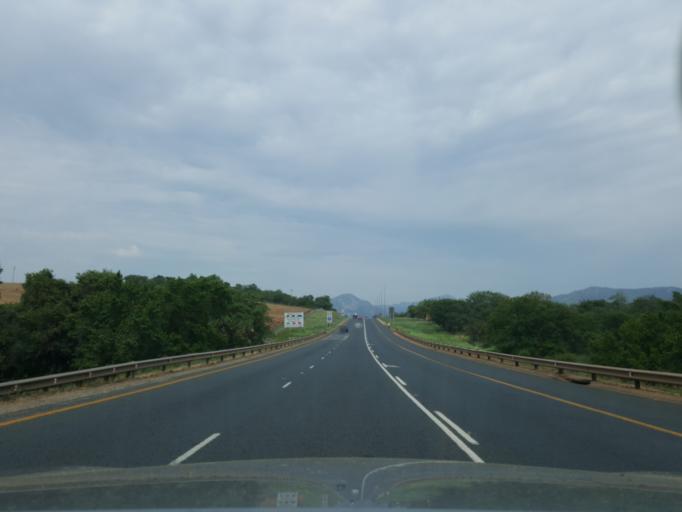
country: SZ
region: Hhohho
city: Ntfonjeni
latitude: -25.5361
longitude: 31.3544
